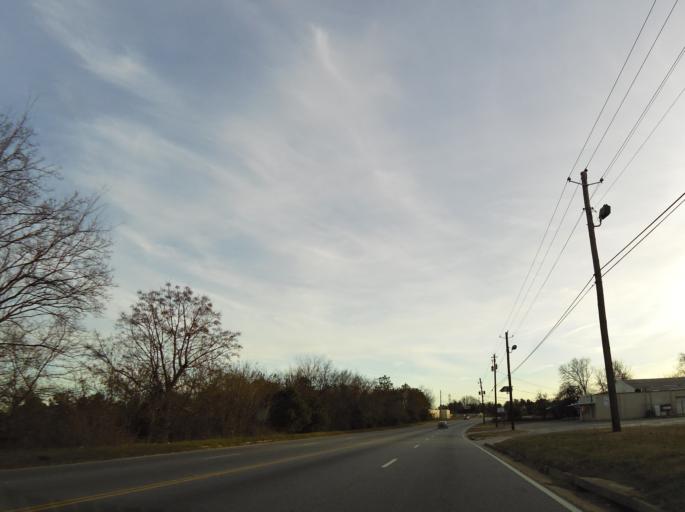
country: US
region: Georgia
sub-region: Bibb County
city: Macon
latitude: 32.8001
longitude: -83.6407
